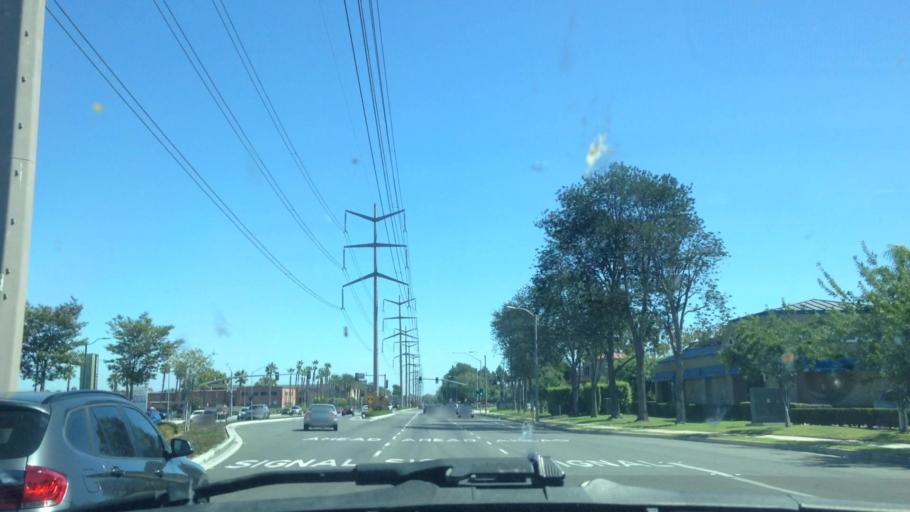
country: US
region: California
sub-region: Orange County
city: Irvine
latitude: 33.6997
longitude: -117.8349
